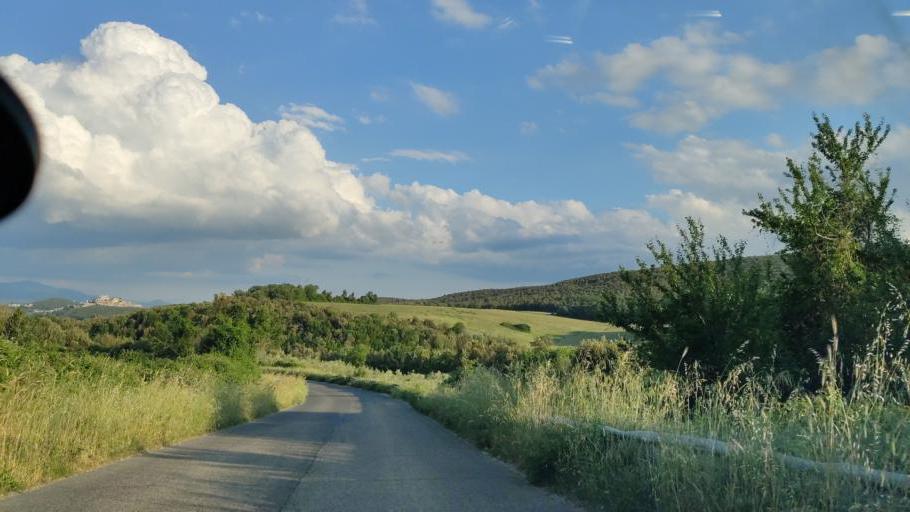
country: IT
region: Umbria
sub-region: Provincia di Terni
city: Amelia
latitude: 42.5824
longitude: 12.3841
